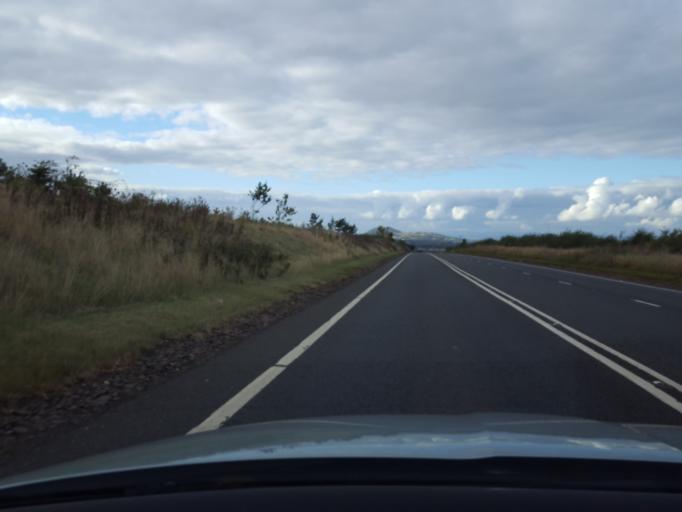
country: GB
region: Scotland
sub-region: Fife
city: Pathhead
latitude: 55.8981
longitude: -3.0150
